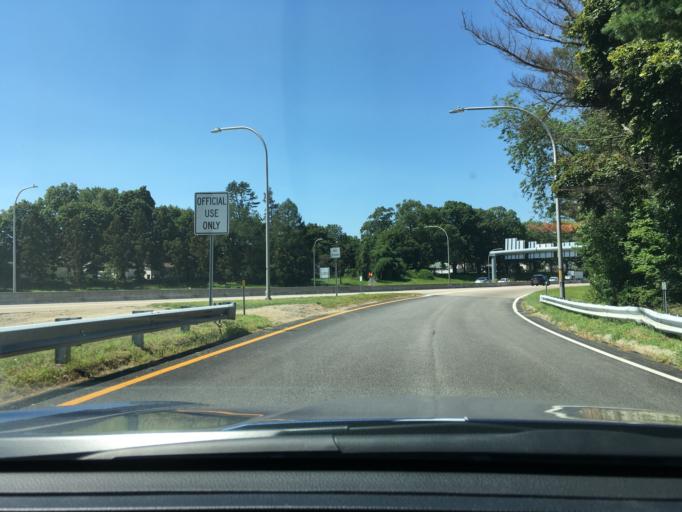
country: US
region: Rhode Island
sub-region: Providence County
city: Cranston
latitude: 41.7824
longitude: -71.4263
